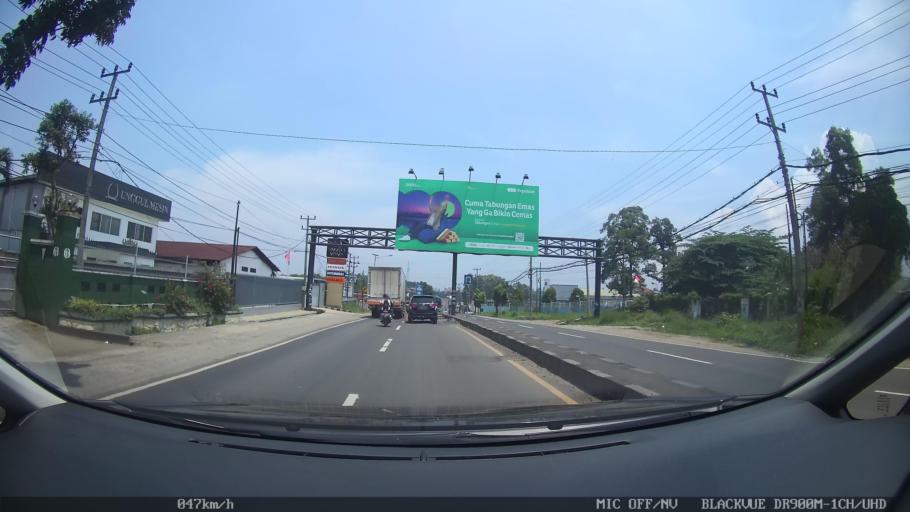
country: ID
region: Lampung
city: Natar
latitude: -5.3392
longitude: 105.2127
